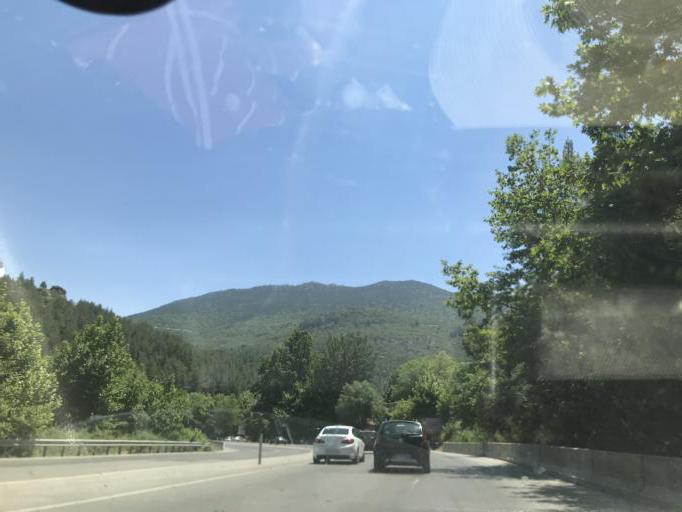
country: TR
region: Denizli
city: Denizli
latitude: 37.7287
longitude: 29.1659
